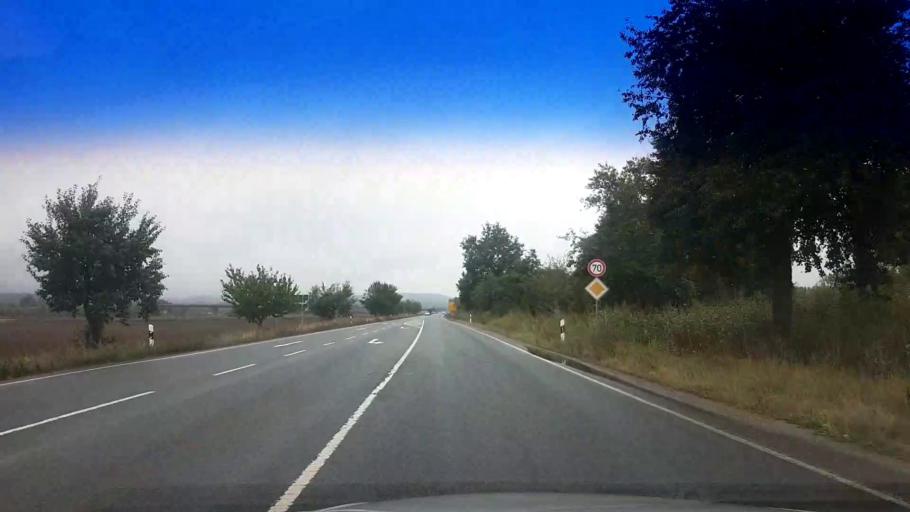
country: DE
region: Bavaria
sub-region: Upper Franconia
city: Eggolsheim
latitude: 49.7663
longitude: 11.0402
